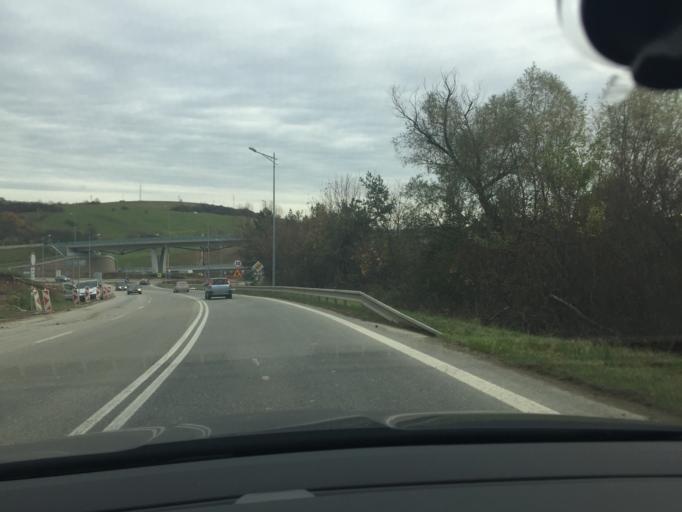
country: SK
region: Presovsky
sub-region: Okres Presov
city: Presov
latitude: 48.9987
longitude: 21.2000
